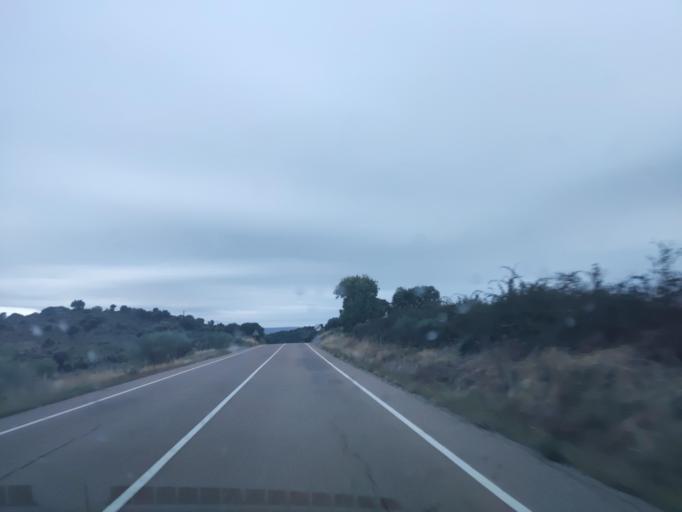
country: ES
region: Castille and Leon
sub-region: Provincia de Salamanca
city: Hinojosa de Duero
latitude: 40.9756
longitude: -6.8299
